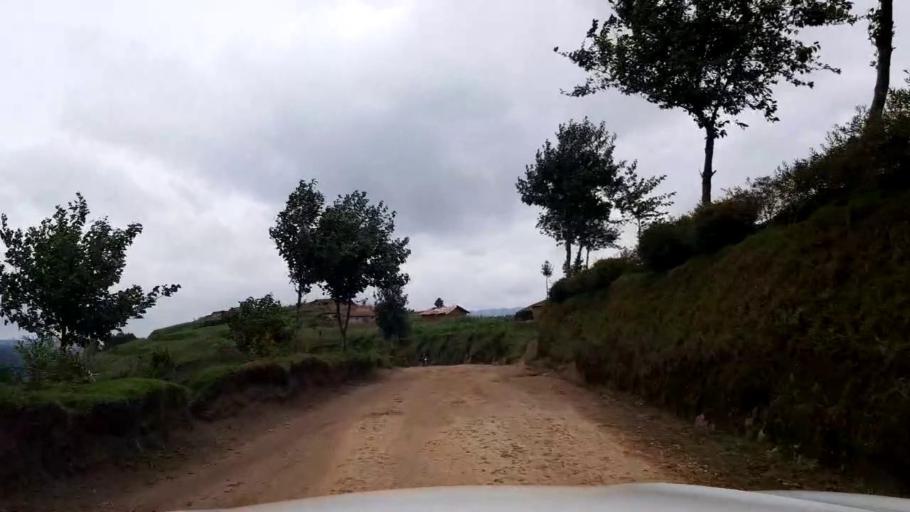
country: RW
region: Western Province
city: Kibuye
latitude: -1.9538
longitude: 29.4141
